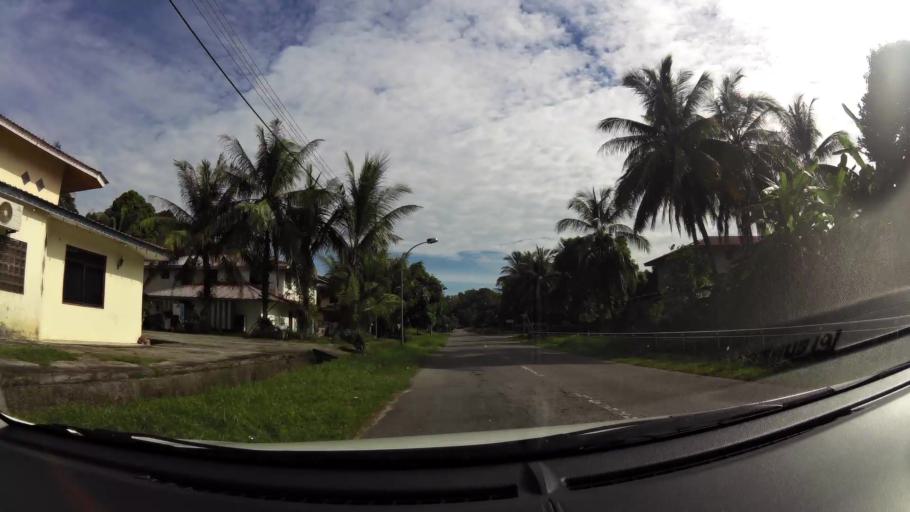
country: BN
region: Brunei and Muara
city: Bandar Seri Begawan
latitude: 4.9192
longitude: 114.8970
